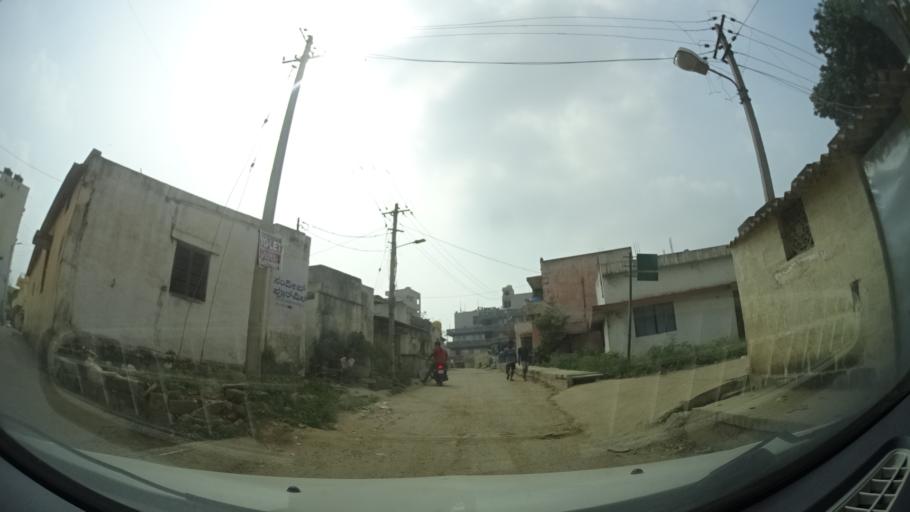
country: IN
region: Karnataka
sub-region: Bangalore Urban
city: Anekal
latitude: 12.8242
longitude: 77.6689
